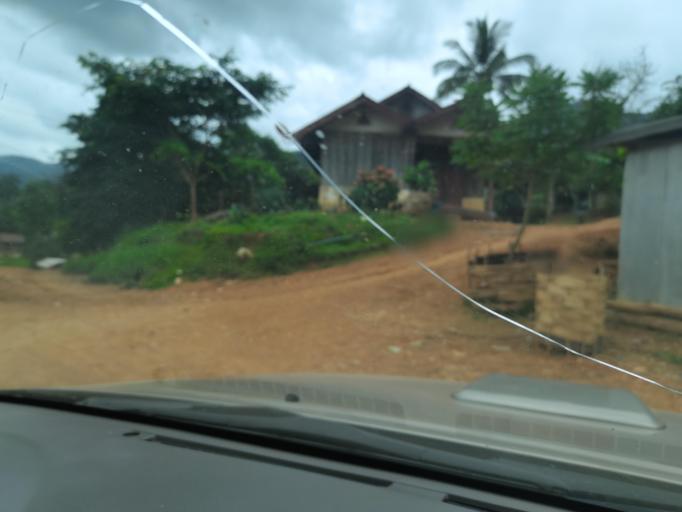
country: TH
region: Phayao
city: Phu Sang
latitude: 19.7470
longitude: 100.4279
